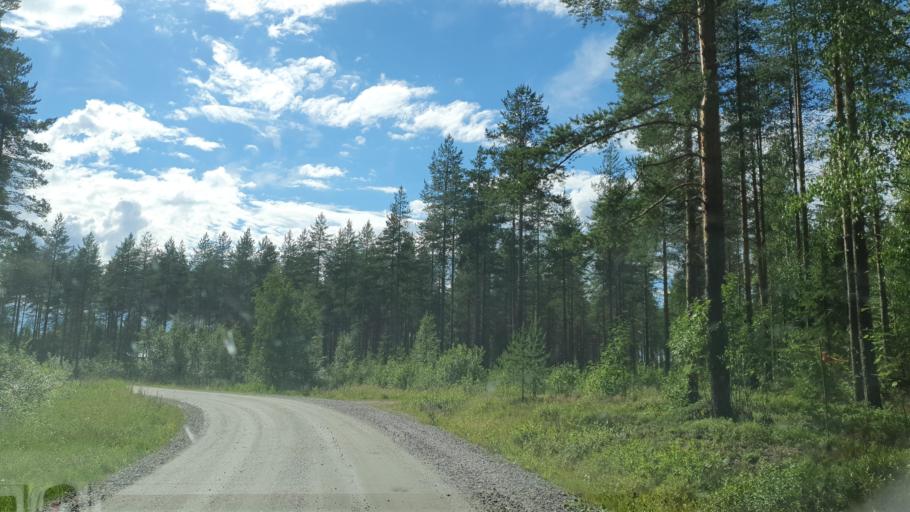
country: FI
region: Kainuu
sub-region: Kehys-Kainuu
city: Kuhmo
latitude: 64.1369
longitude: 29.6718
